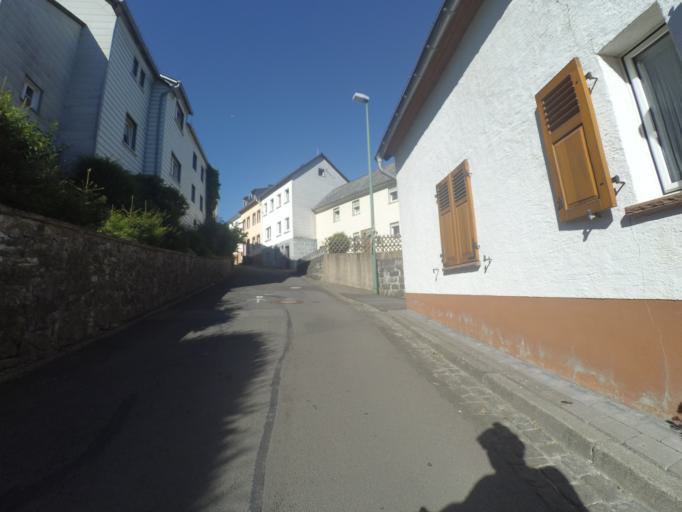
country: DE
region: Rheinland-Pfalz
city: Daun
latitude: 50.1980
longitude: 6.8309
